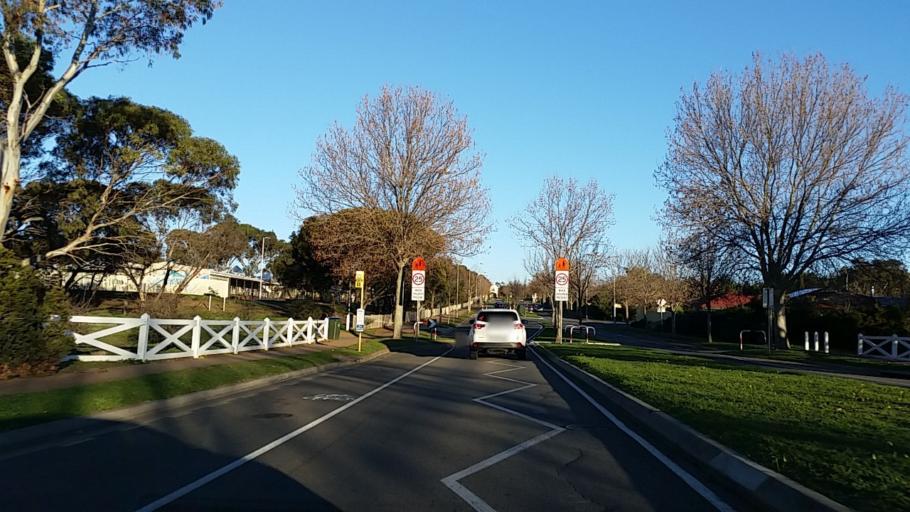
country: AU
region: South Australia
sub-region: Onkaparinga
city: Moana
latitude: -35.1985
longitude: 138.4858
